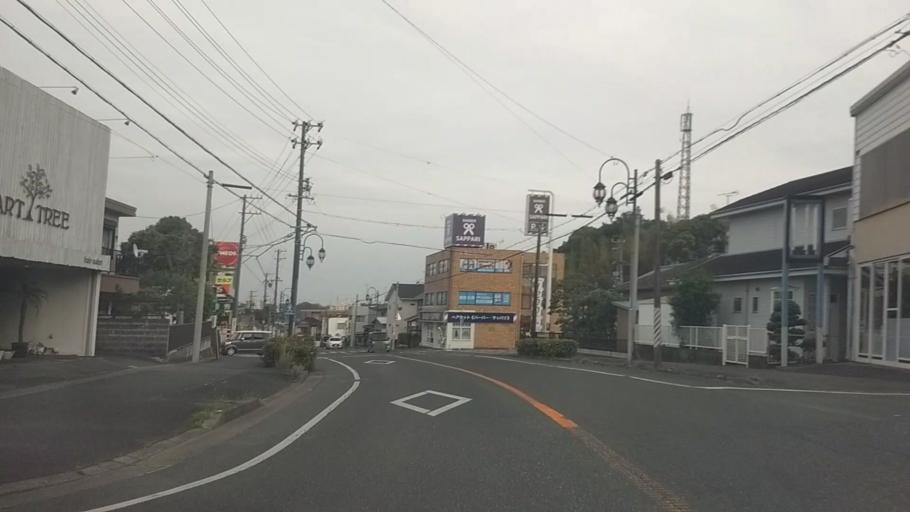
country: JP
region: Shizuoka
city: Hamamatsu
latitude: 34.7280
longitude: 137.6908
